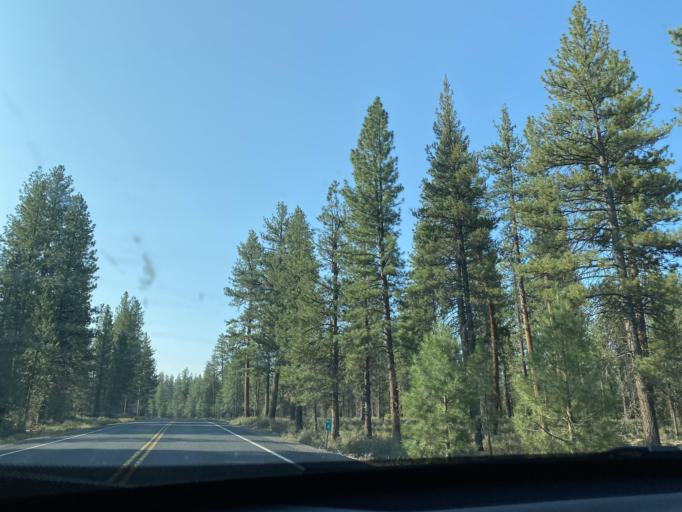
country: US
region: Oregon
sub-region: Deschutes County
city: La Pine
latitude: 43.7149
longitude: -121.4125
